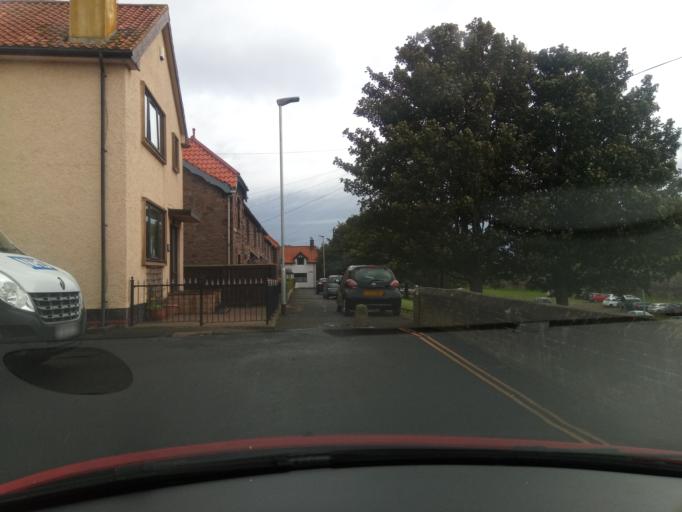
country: GB
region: England
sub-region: Northumberland
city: Berwick-Upon-Tweed
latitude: 55.7731
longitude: -2.0045
